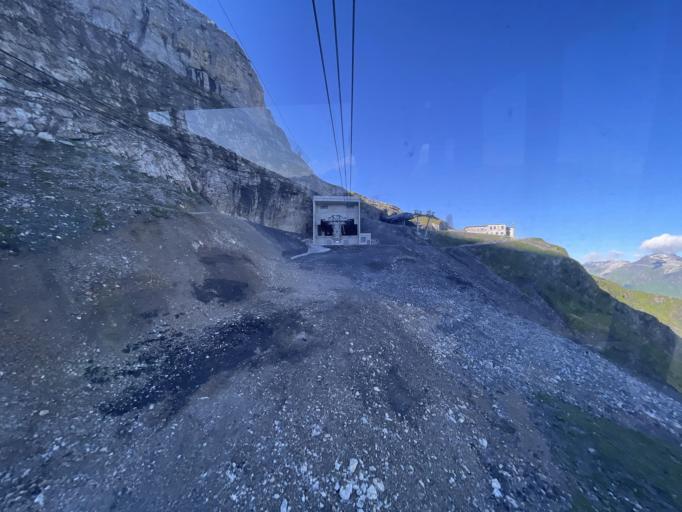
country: CH
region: Bern
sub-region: Interlaken-Oberhasli District
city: Lauterbrunnen
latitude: 46.5766
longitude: 7.9768
